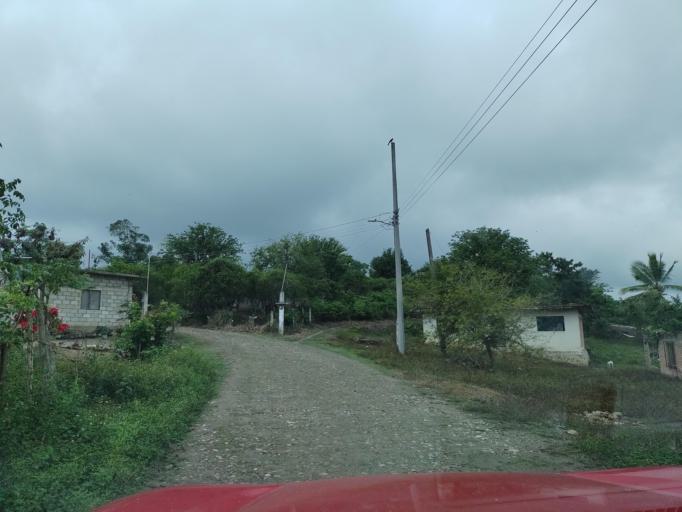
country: MX
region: Veracruz
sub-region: Papantla
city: El Chote
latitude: 20.4139
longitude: -97.3673
